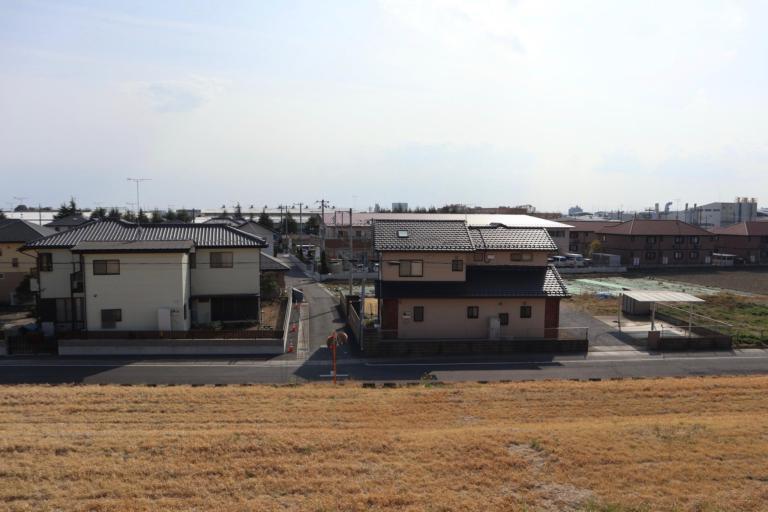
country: JP
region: Tochigi
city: Ashikaga
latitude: 36.3145
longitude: 139.4717
